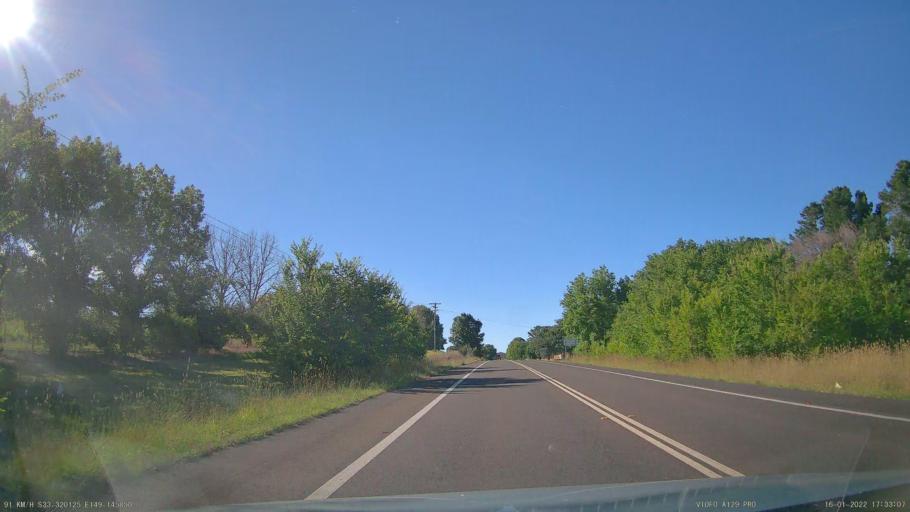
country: AU
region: New South Wales
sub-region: Orange Municipality
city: Orange
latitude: -33.3199
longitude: 149.1457
